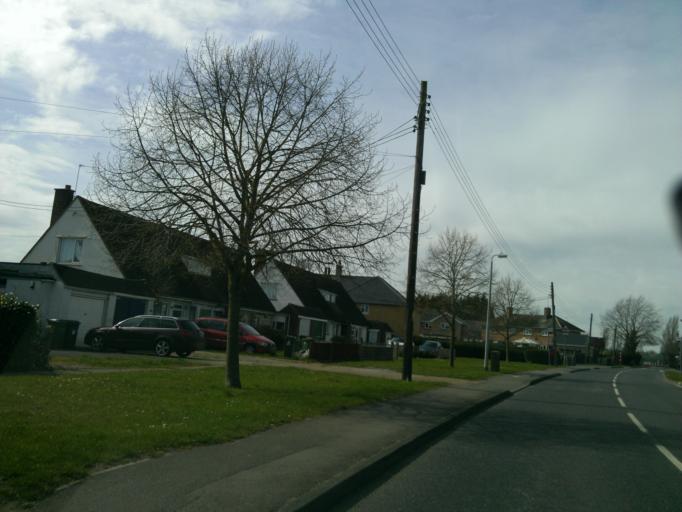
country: GB
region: England
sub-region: Essex
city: Witham
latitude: 51.8436
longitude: 0.6296
